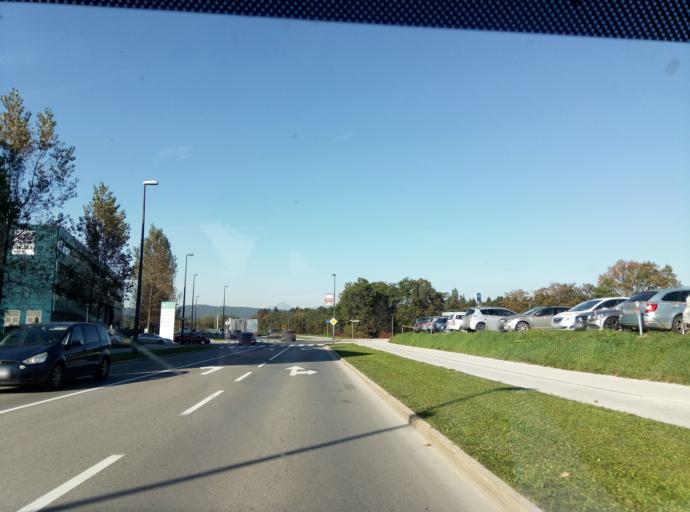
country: SI
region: Ljubljana
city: Ljubljana
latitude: 46.0491
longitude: 14.4612
